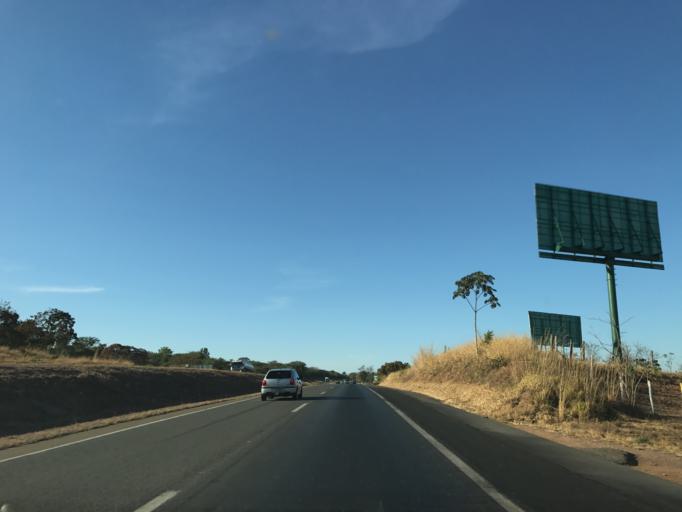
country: BR
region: Goias
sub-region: Hidrolandia
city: Hidrolandia
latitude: -16.9040
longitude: -49.2544
